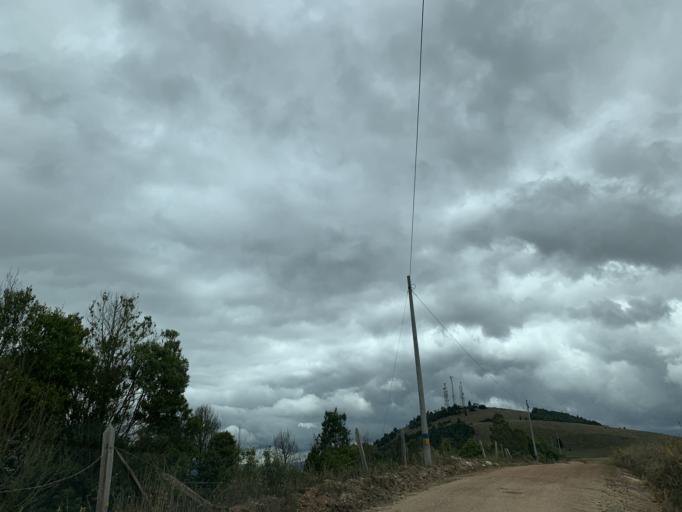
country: CO
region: Boyaca
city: Tunja
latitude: 5.5346
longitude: -73.3213
